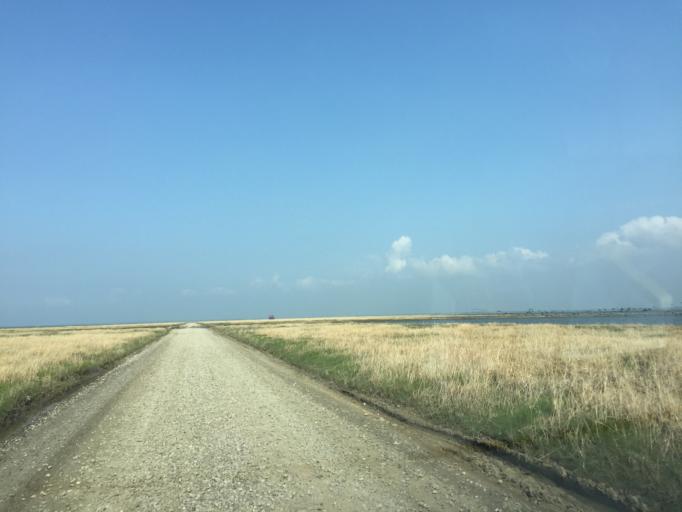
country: DK
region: South Denmark
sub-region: Esbjerg Kommune
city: Ribe
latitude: 55.2974
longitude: 8.6081
